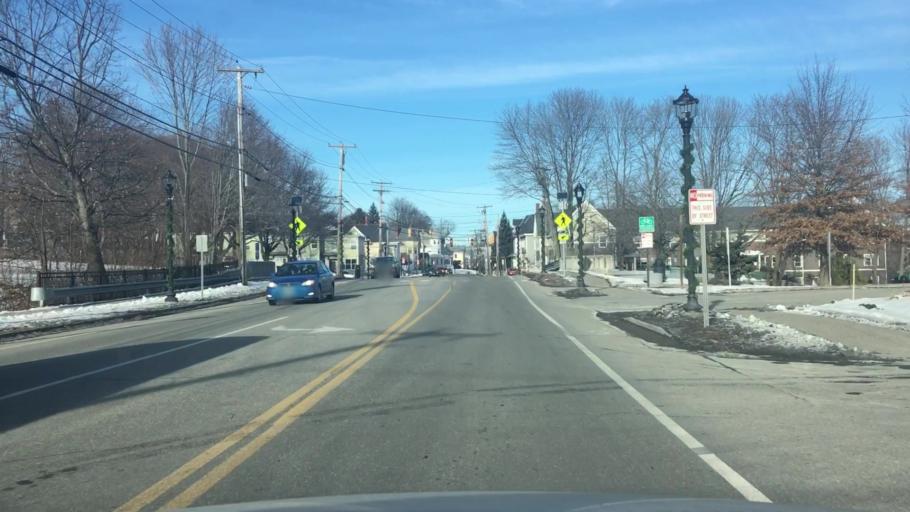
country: US
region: Maine
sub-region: Androscoggin County
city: Auburn
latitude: 44.0914
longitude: -70.2261
